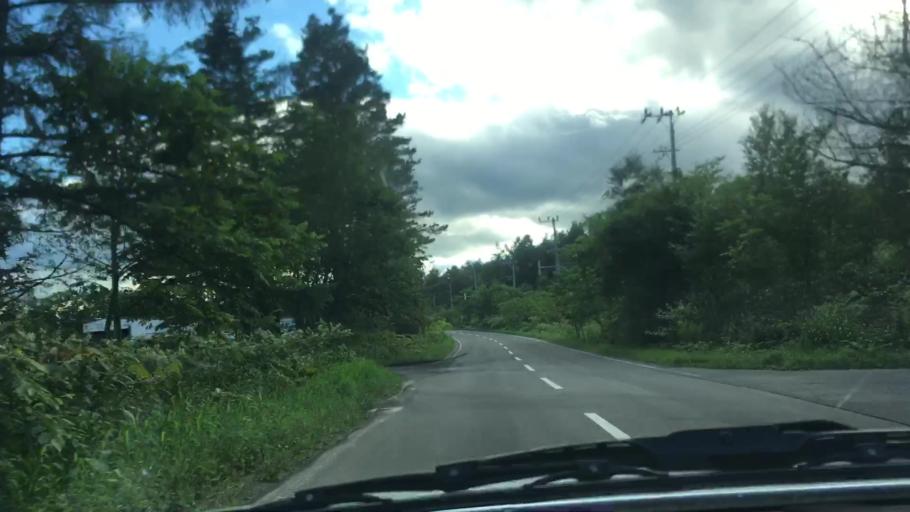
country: JP
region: Hokkaido
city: Otofuke
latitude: 43.1717
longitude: 142.9145
